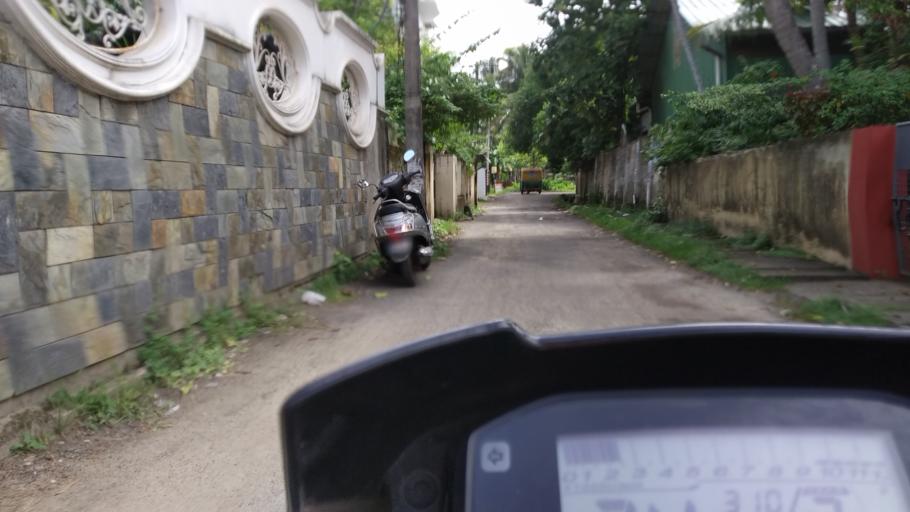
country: IN
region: Kerala
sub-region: Ernakulam
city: Cochin
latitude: 9.9873
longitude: 76.3038
